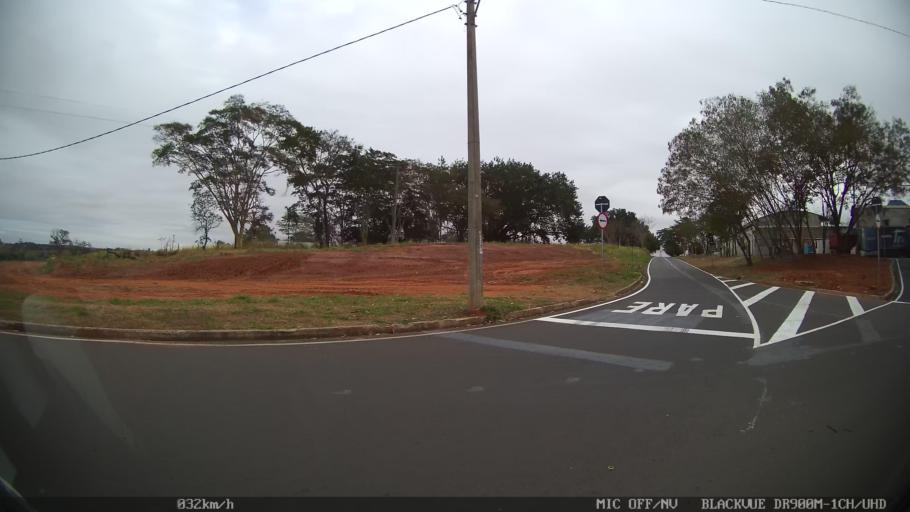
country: BR
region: Sao Paulo
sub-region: Sao Jose Do Rio Preto
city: Sao Jose do Rio Preto
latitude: -20.8305
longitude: -49.4259
